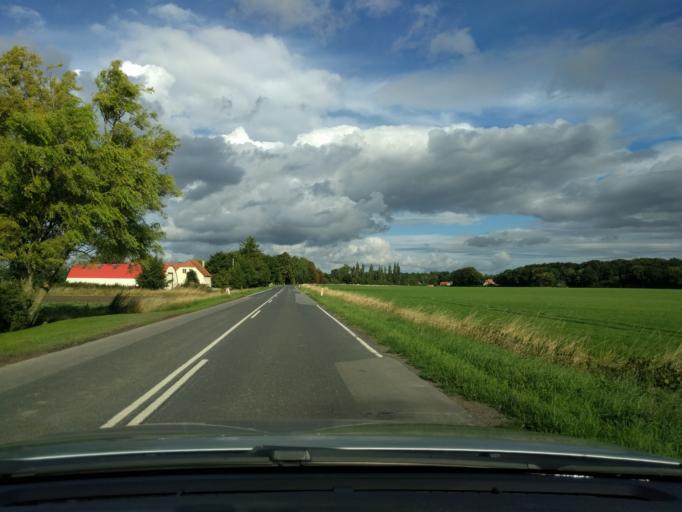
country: DK
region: South Denmark
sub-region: Kerteminde Kommune
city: Kerteminde
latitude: 55.4048
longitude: 10.6653
